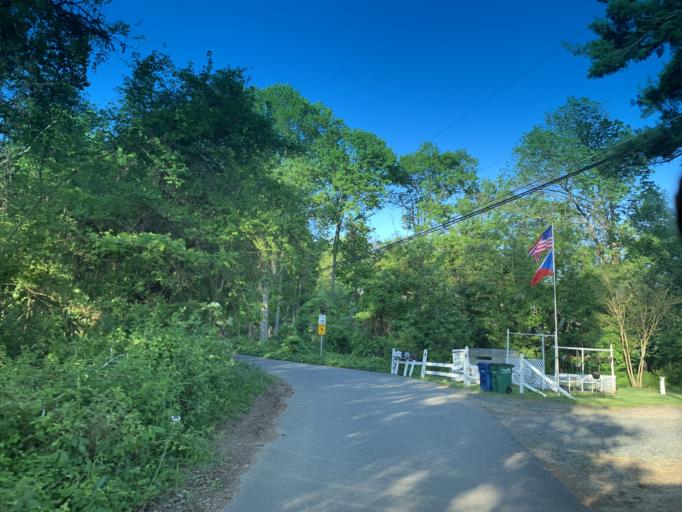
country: US
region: Maryland
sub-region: Harford County
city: Aberdeen
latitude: 39.5215
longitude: -76.1955
